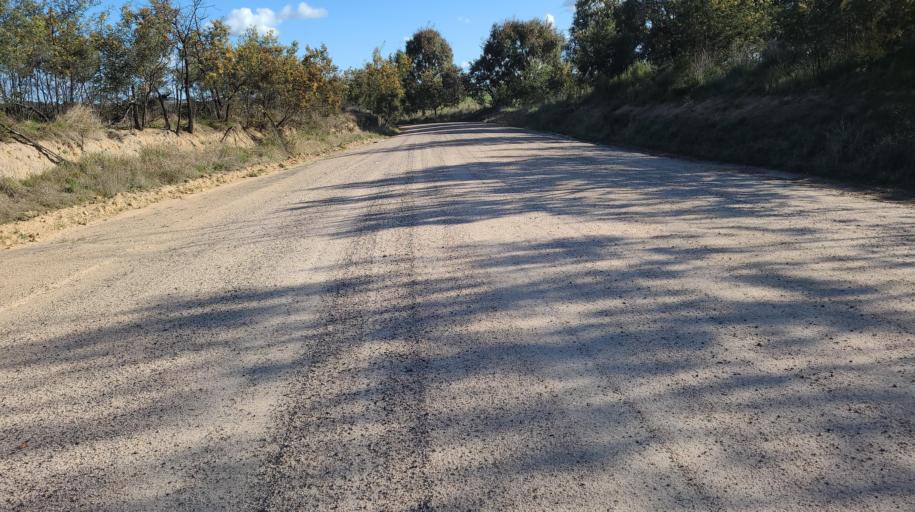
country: AU
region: New South Wales
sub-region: Blayney
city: Millthorpe
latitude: -33.3931
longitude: 149.3101
